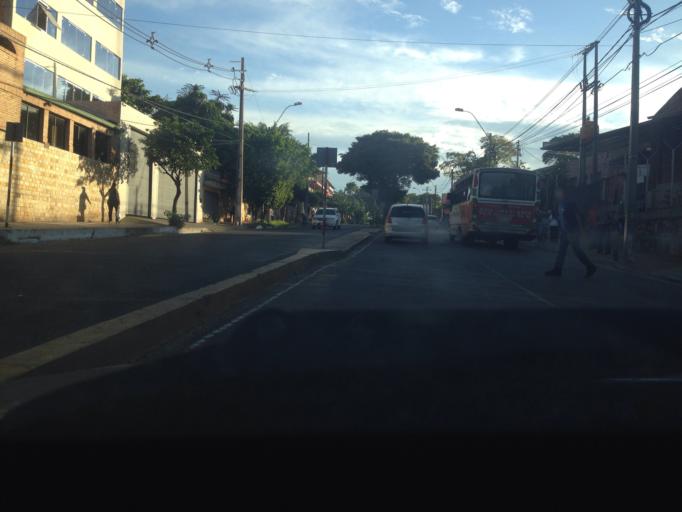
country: PY
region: Central
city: Lambare
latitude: -25.3132
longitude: -57.5880
